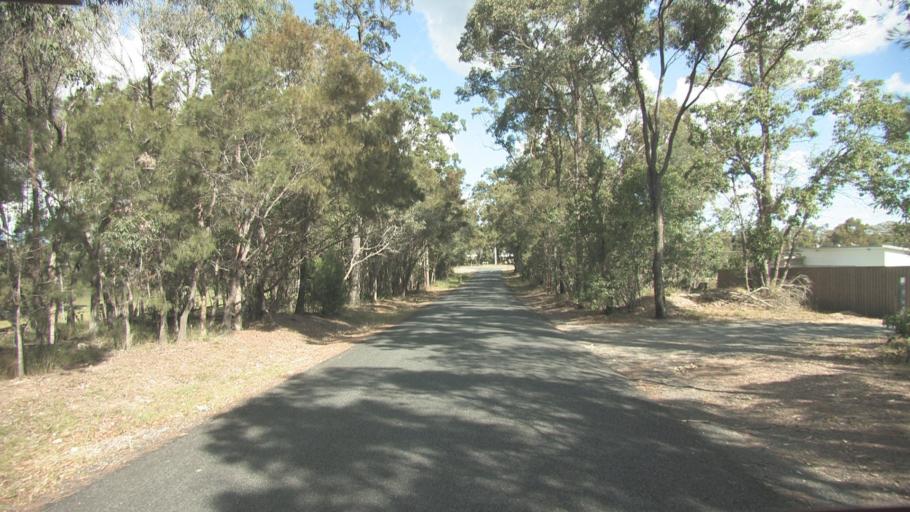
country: AU
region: Queensland
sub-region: Logan
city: Beenleigh
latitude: -27.6559
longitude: 153.2295
